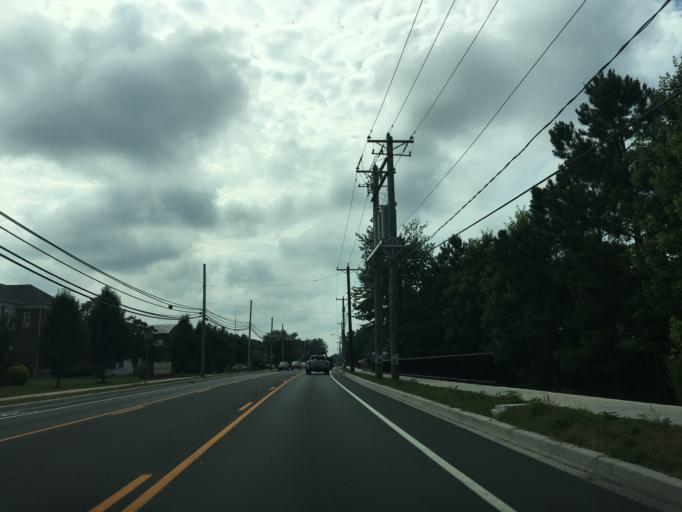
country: US
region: Delaware
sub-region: Sussex County
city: Ocean View
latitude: 38.5455
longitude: -75.0989
